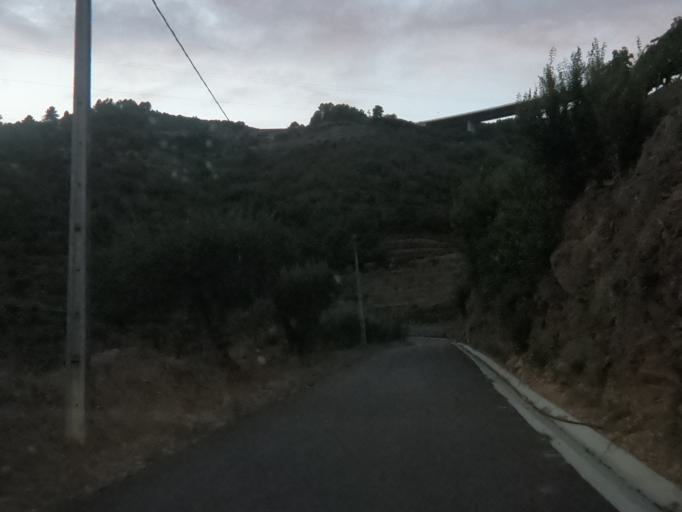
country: PT
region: Vila Real
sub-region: Vila Real
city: Vila Real
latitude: 41.2746
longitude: -7.7607
